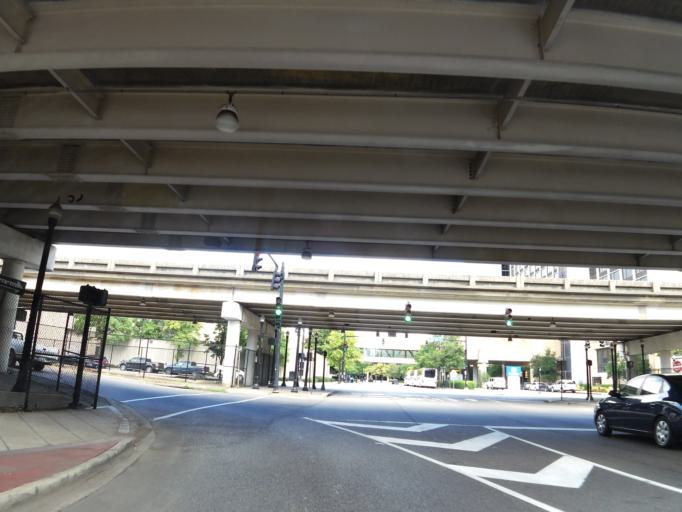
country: US
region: Alabama
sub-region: Jefferson County
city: Birmingham
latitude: 33.5232
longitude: -86.8098
